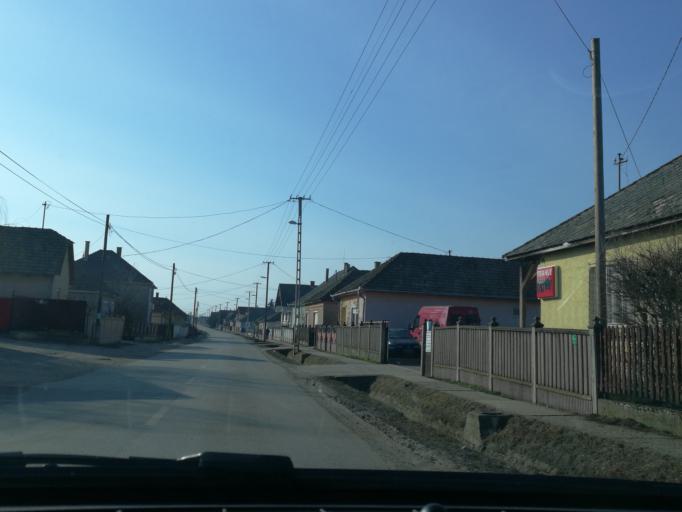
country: HU
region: Szabolcs-Szatmar-Bereg
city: Apagy
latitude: 48.0178
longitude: 21.9614
